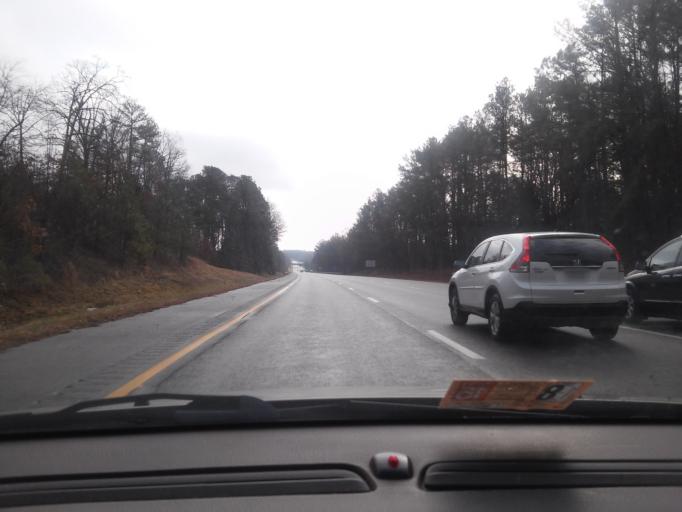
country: US
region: Virginia
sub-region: Henrico County
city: Short Pump
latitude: 37.6415
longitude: -77.5862
